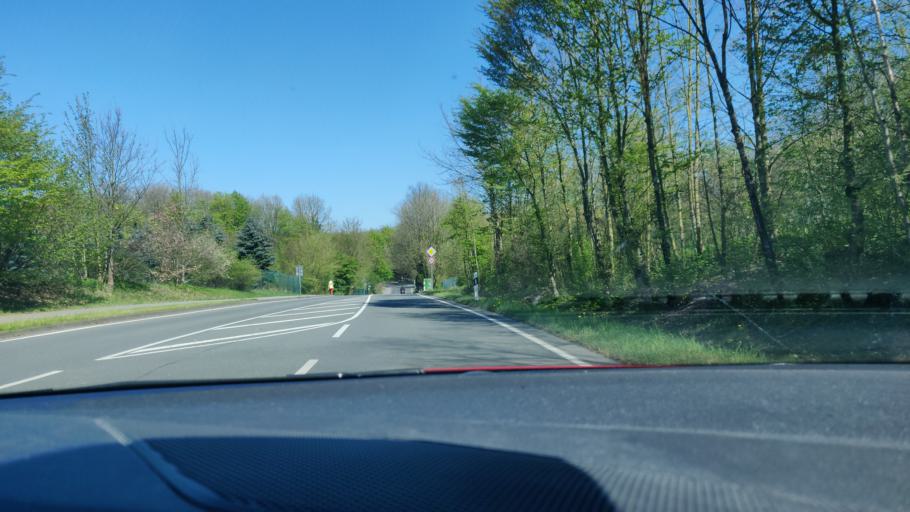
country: DE
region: North Rhine-Westphalia
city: Wulfrath
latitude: 51.2696
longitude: 7.0728
